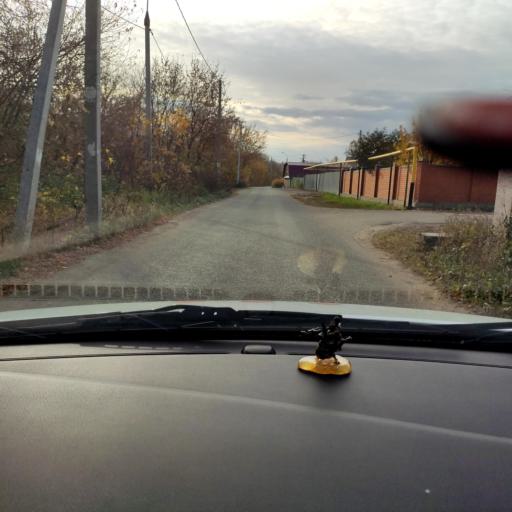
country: RU
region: Tatarstan
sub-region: Gorod Kazan'
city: Kazan
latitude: 55.7368
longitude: 49.0976
